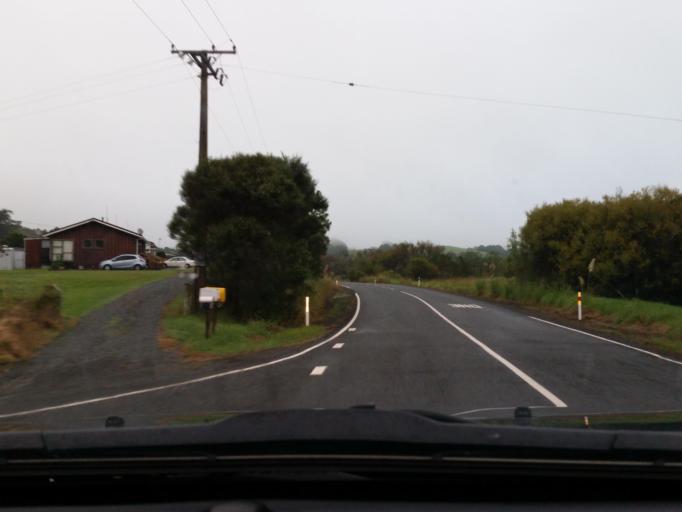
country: NZ
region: Northland
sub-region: Whangarei
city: Maungatapere
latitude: -35.8281
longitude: 174.0474
